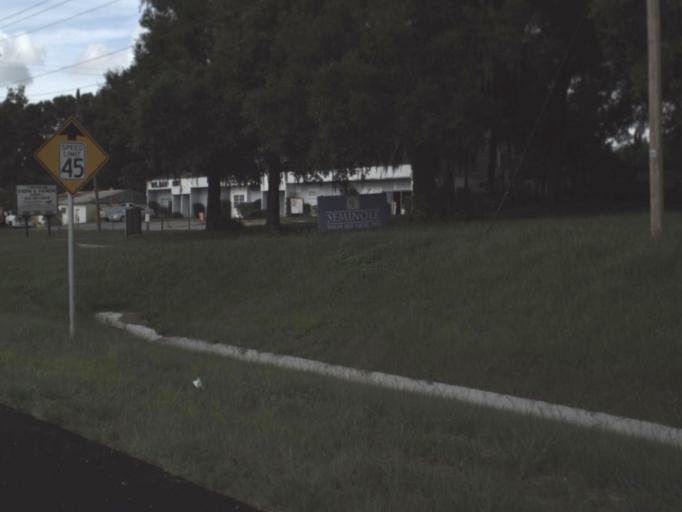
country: US
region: Florida
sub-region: Pasco County
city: Dade City North
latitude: 28.3902
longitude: -82.1946
